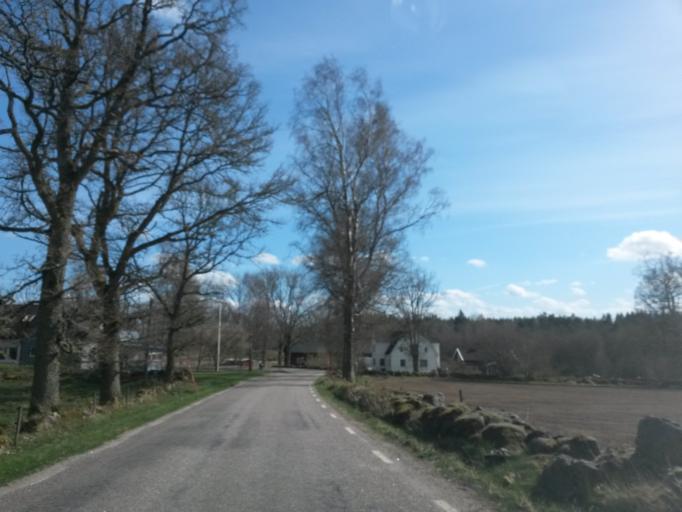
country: SE
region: Vaestra Goetaland
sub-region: Vargarda Kommun
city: Jonstorp
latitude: 57.9979
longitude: 12.7618
